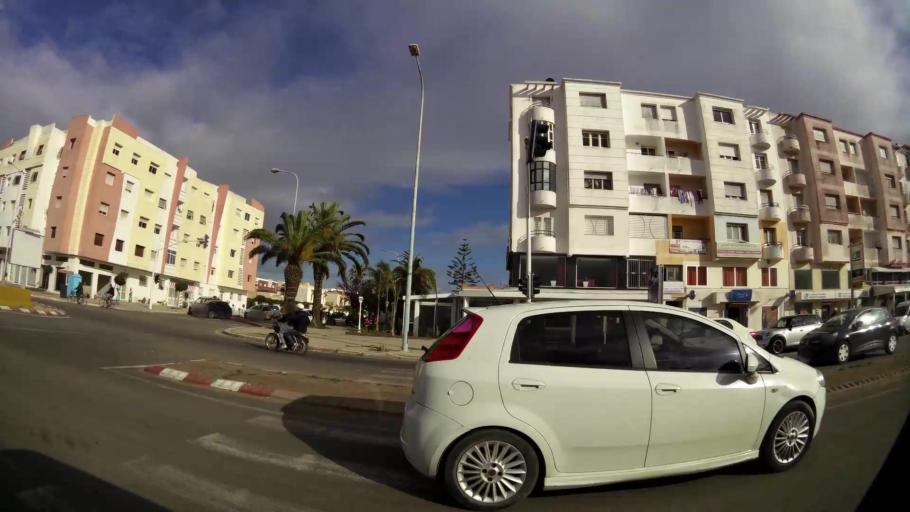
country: MA
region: Doukkala-Abda
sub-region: El-Jadida
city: El Jadida
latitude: 33.2450
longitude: -8.5206
